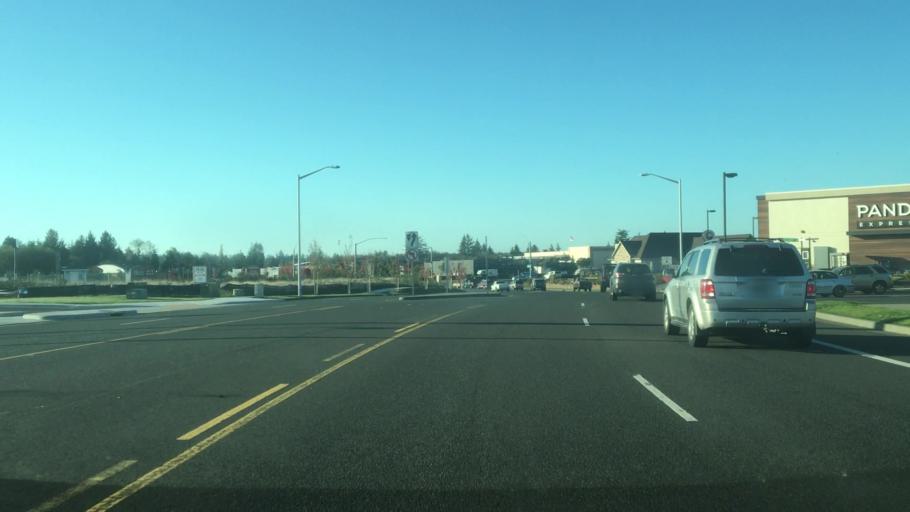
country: US
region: Oregon
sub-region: Clatsop County
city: Warrenton
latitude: 46.1458
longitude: -123.9155
